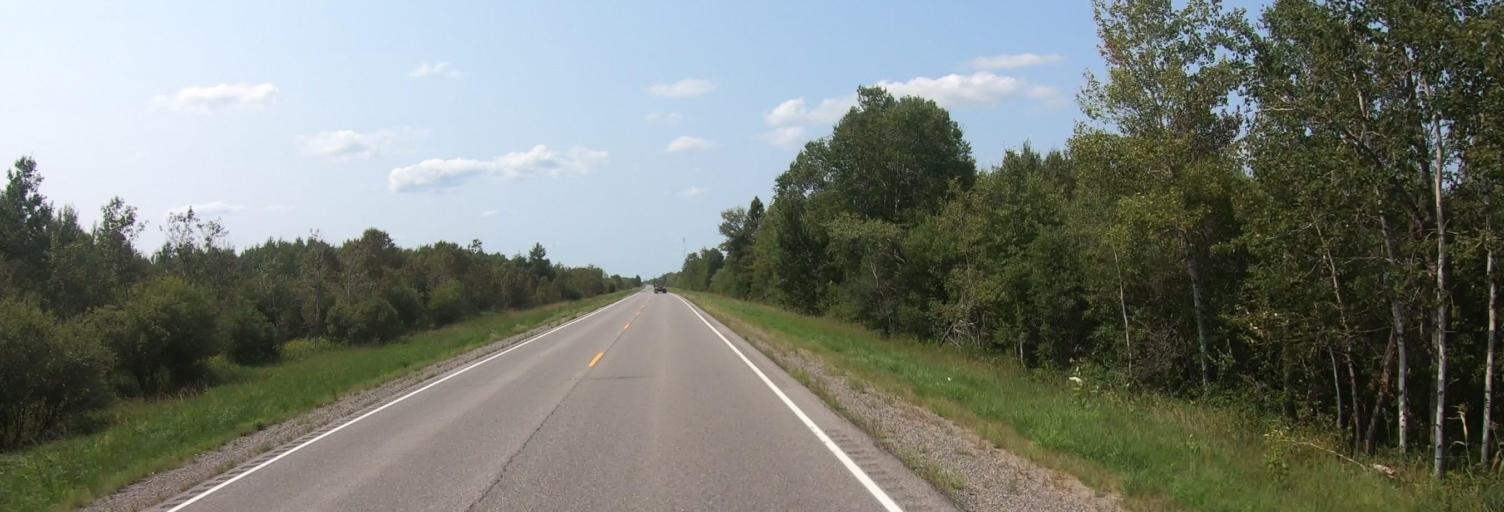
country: US
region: Minnesota
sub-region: Koochiching County
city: International Falls
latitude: 48.6287
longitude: -93.9942
